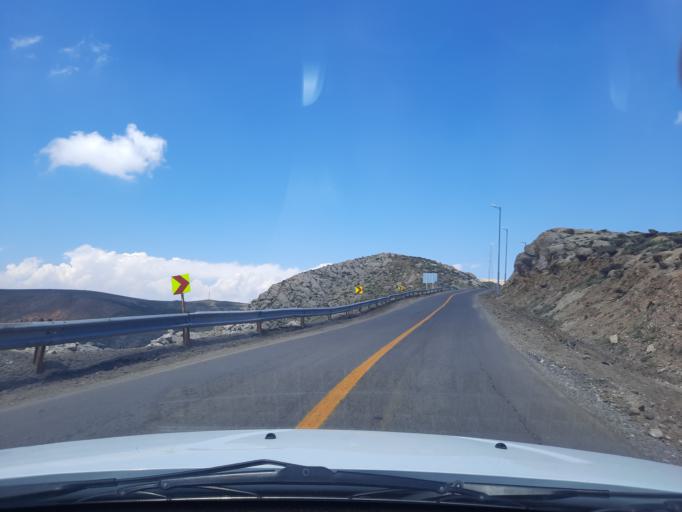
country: IR
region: Qazvin
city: Qazvin
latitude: 36.3806
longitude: 50.2019
